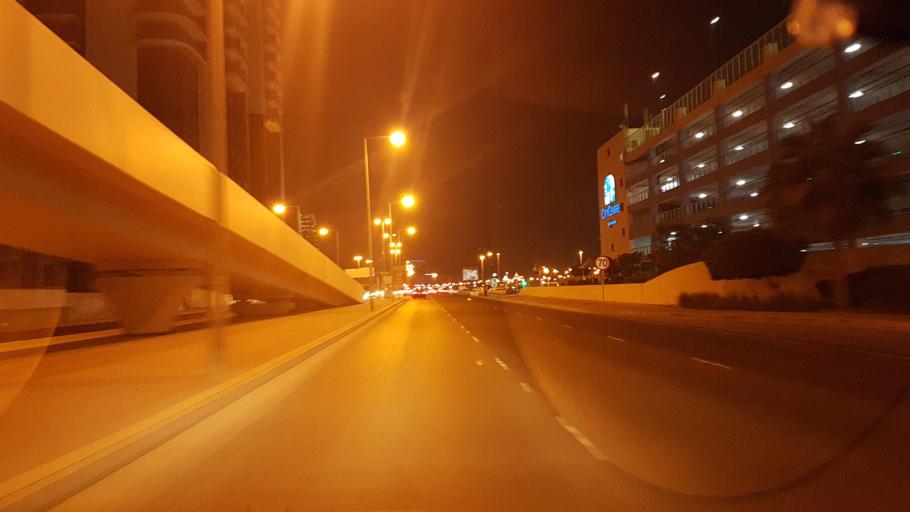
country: BH
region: Manama
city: Jidd Hafs
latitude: 26.2350
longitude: 50.5544
